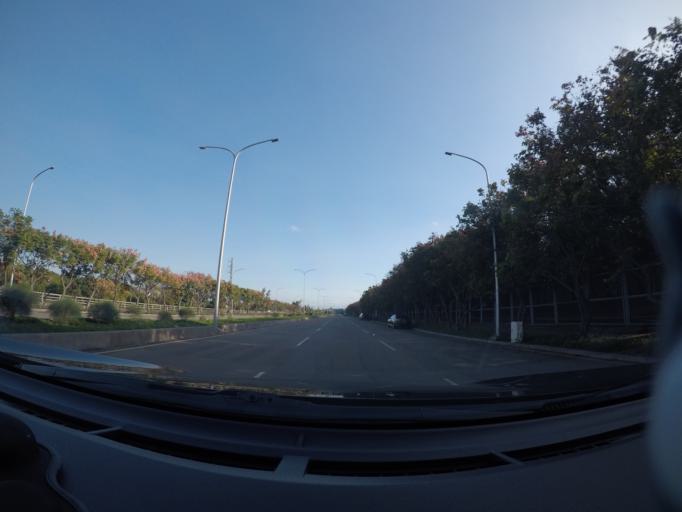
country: TW
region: Taiwan
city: Taoyuan City
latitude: 25.0990
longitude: 121.2553
